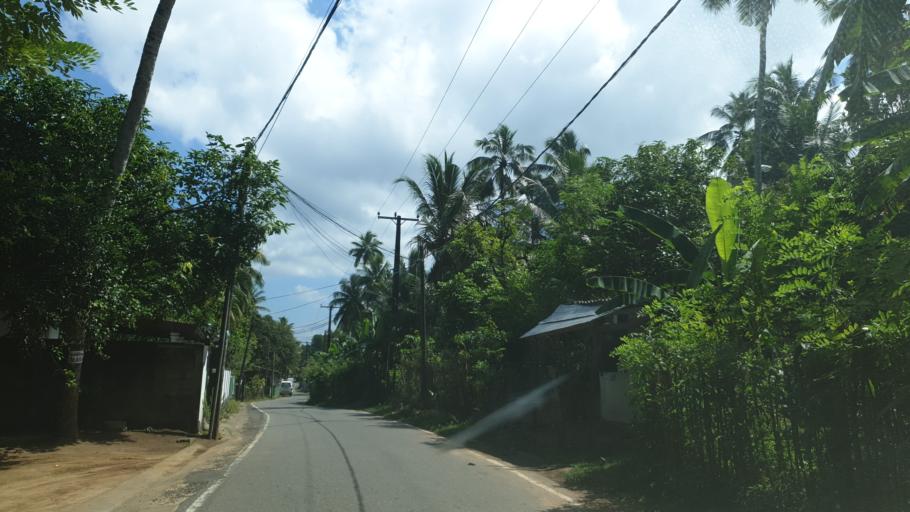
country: LK
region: Western
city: Panadura
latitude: 6.6740
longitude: 79.9350
